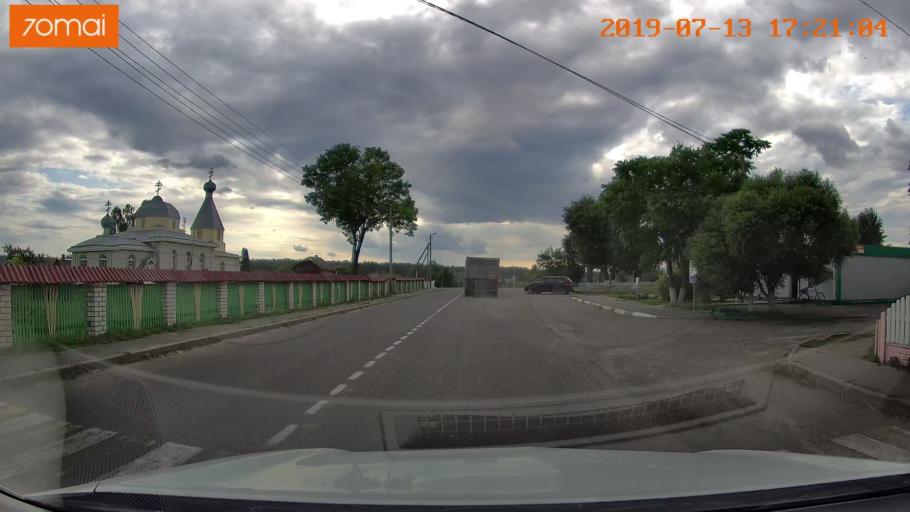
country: BY
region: Mogilev
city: Babruysk
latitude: 53.2727
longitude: 29.2433
